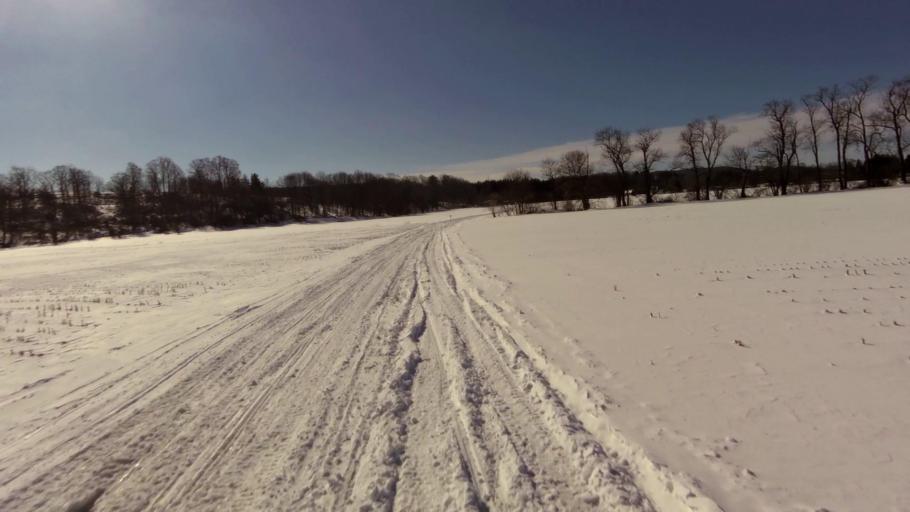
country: US
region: New York
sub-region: Cattaraugus County
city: Franklinville
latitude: 42.3494
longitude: -78.4486
